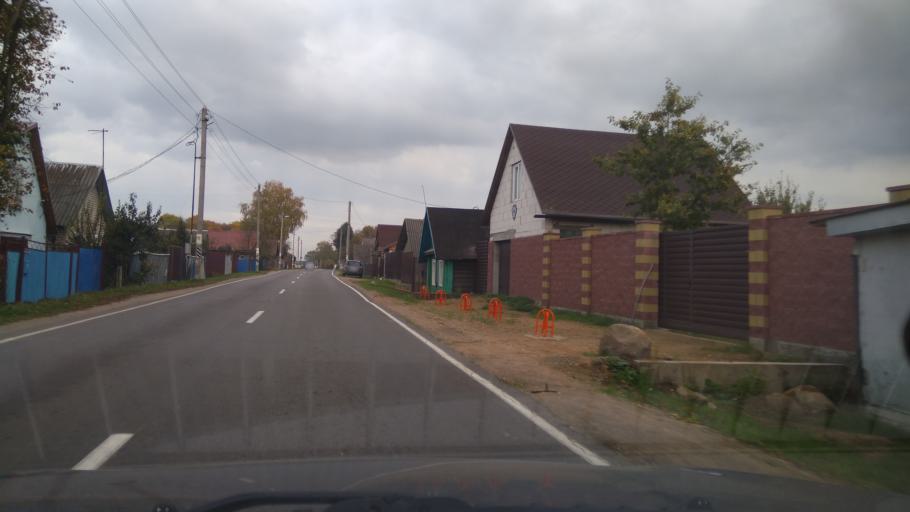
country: BY
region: Minsk
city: Dukora
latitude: 53.6691
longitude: 27.9485
